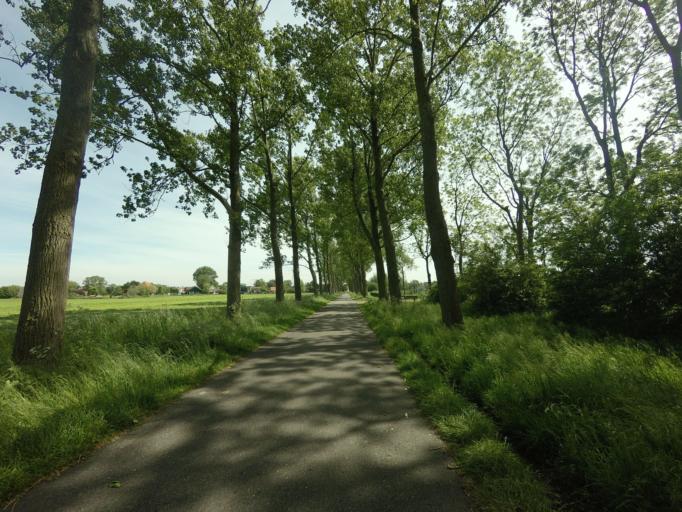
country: NL
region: North Holland
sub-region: Gemeente Uitgeest
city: Uitgeest
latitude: 52.4582
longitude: 4.7305
